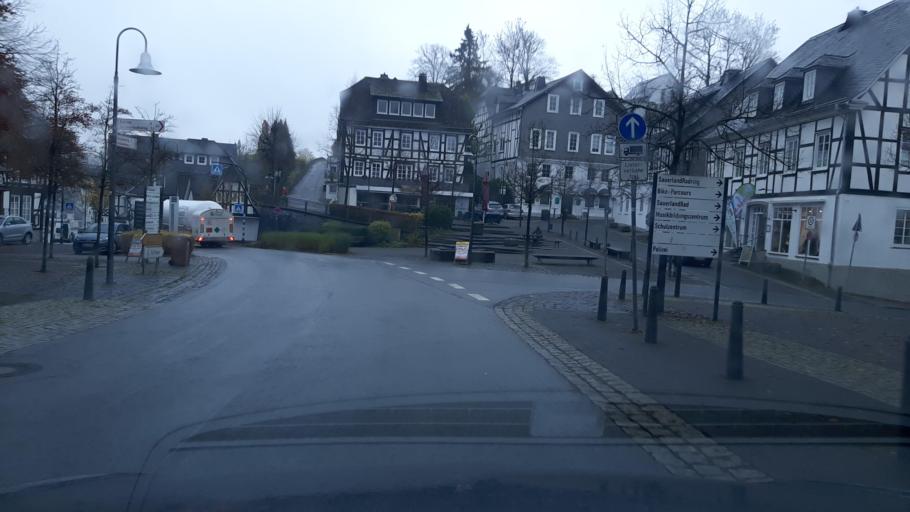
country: DE
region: North Rhine-Westphalia
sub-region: Regierungsbezirk Arnsberg
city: Bad Fredeburg
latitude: 51.1917
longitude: 8.3108
